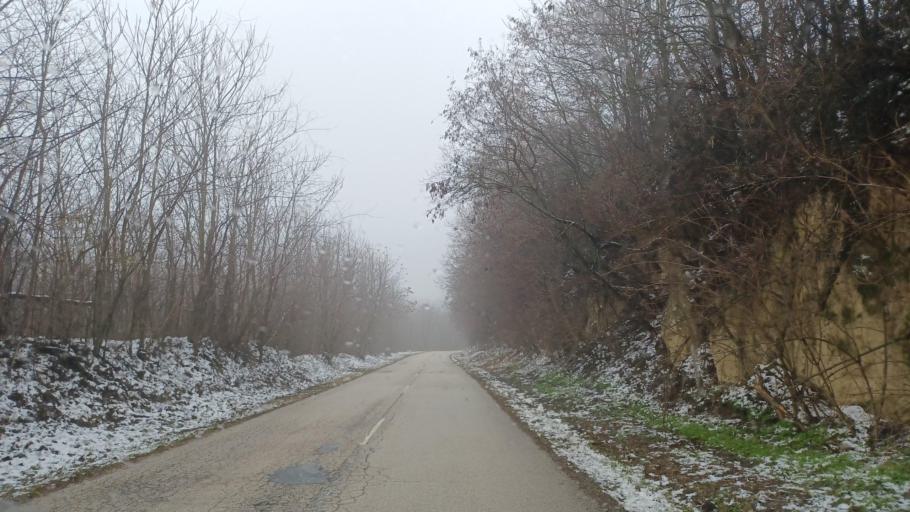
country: HU
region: Tolna
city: Gyonk
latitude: 46.6119
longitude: 18.4822
